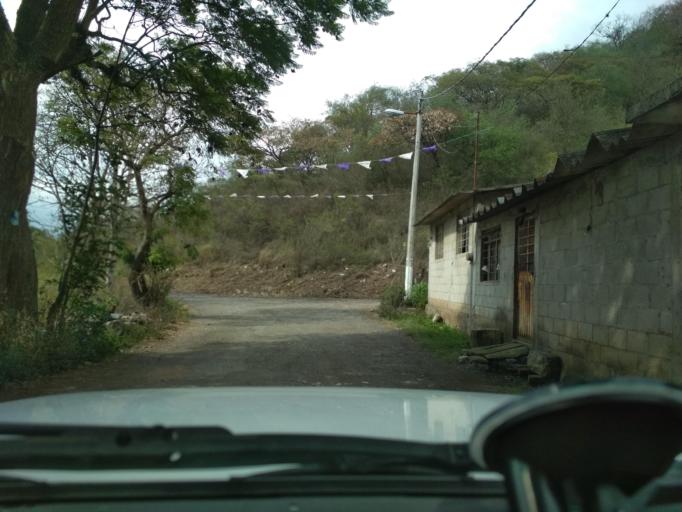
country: MX
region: Veracruz
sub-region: Nogales
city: Taza de Agua Ojo Zarco
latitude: 18.7814
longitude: -97.2005
